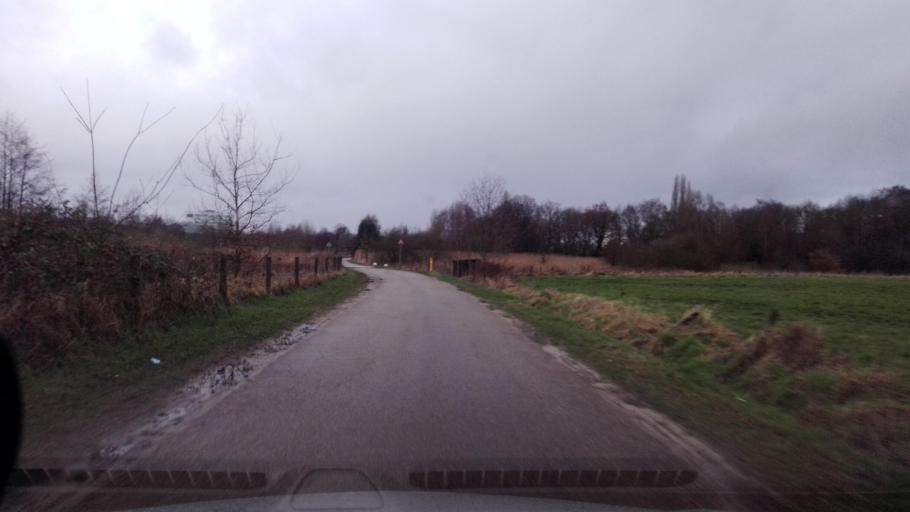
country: NL
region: Limburg
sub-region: Gemeente Venlo
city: Tegelen
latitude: 51.3441
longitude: 6.1617
